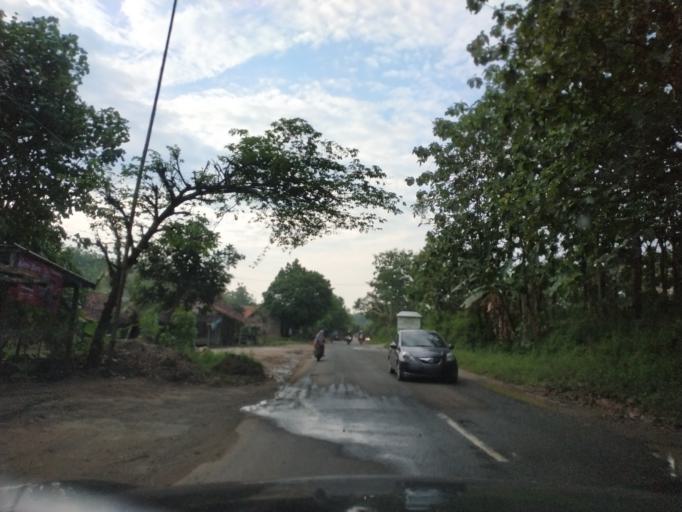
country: ID
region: Central Java
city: Ngampel
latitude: -6.8968
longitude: 111.4401
